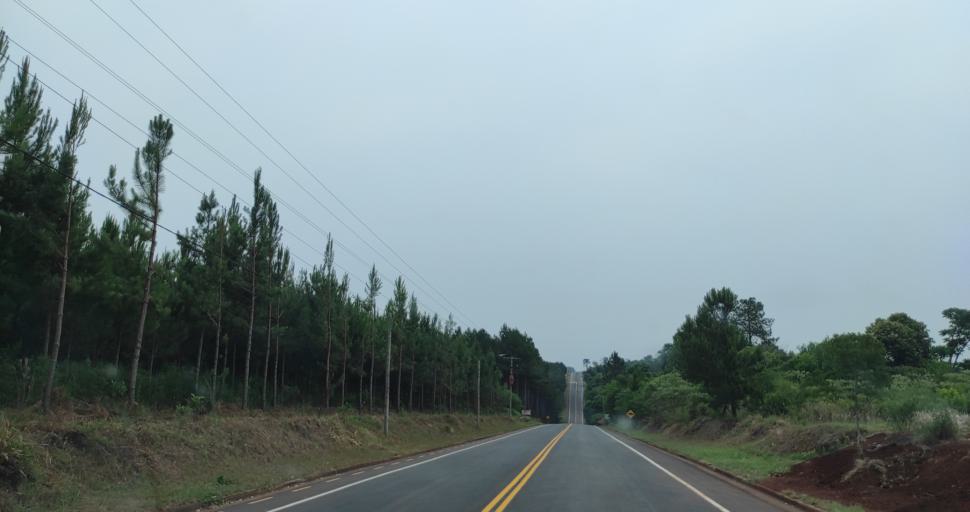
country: AR
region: Misiones
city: Capiovi
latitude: -26.9451
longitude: -55.0546
